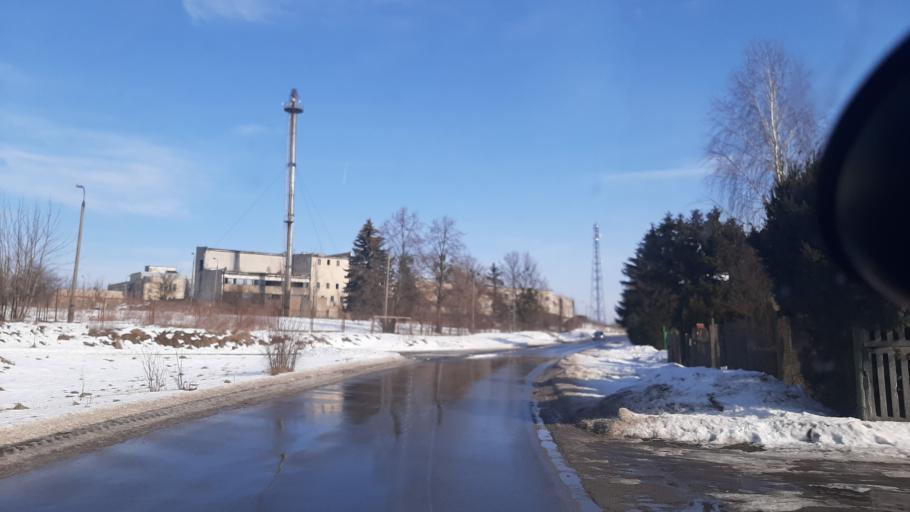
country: PL
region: Lublin Voivodeship
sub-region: Powiat pulawski
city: Kurow
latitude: 51.3853
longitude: 22.1684
